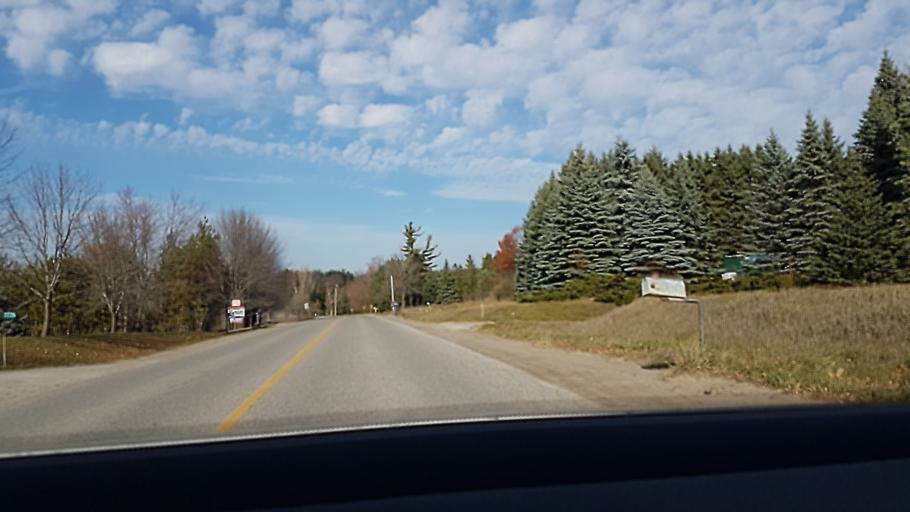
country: CA
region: Ontario
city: Bradford West Gwillimbury
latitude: 44.0477
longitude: -79.7735
